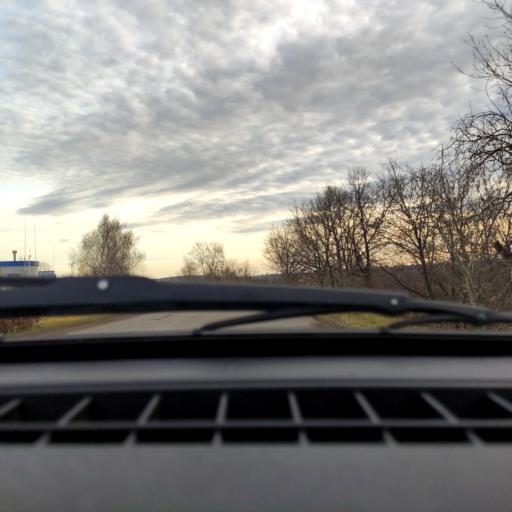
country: RU
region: Bashkortostan
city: Ufa
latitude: 54.8759
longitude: 56.1291
